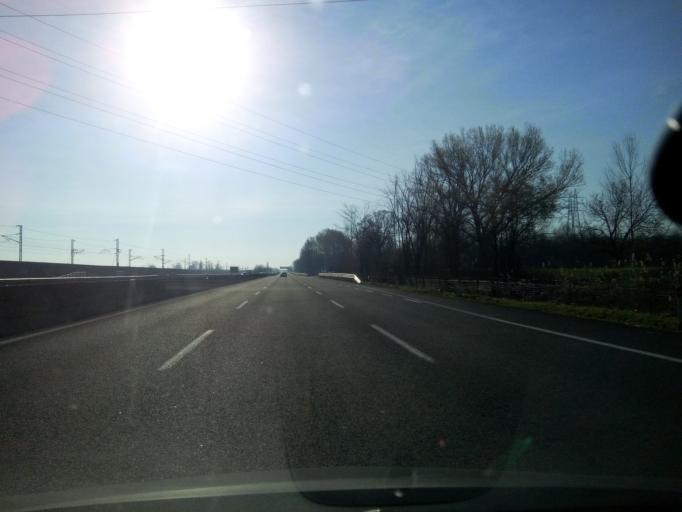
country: IT
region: Emilia-Romagna
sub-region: Provincia di Modena
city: Campogalliano
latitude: 44.6792
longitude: 10.8110
